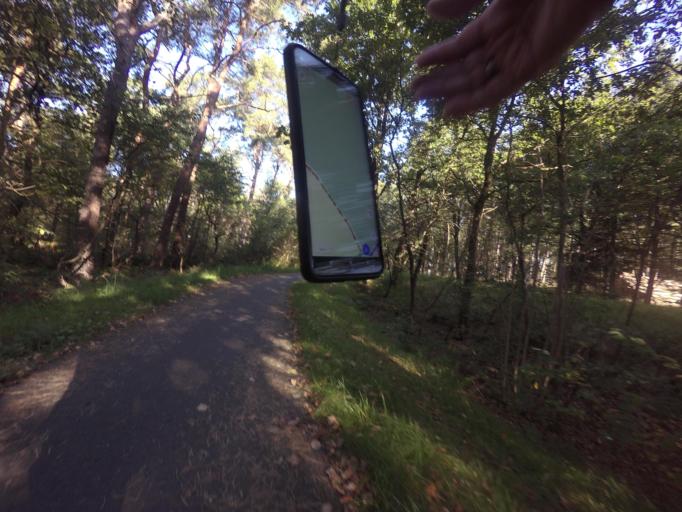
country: DE
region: Lower Saxony
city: Wielen
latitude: 52.5406
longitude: 6.7005
